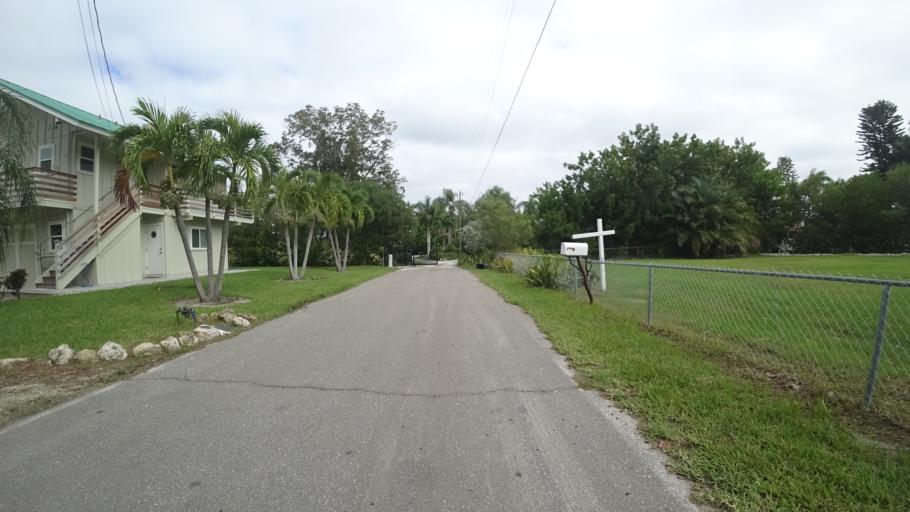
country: US
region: Florida
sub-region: Manatee County
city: Longboat Key
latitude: 27.4300
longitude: -82.6757
